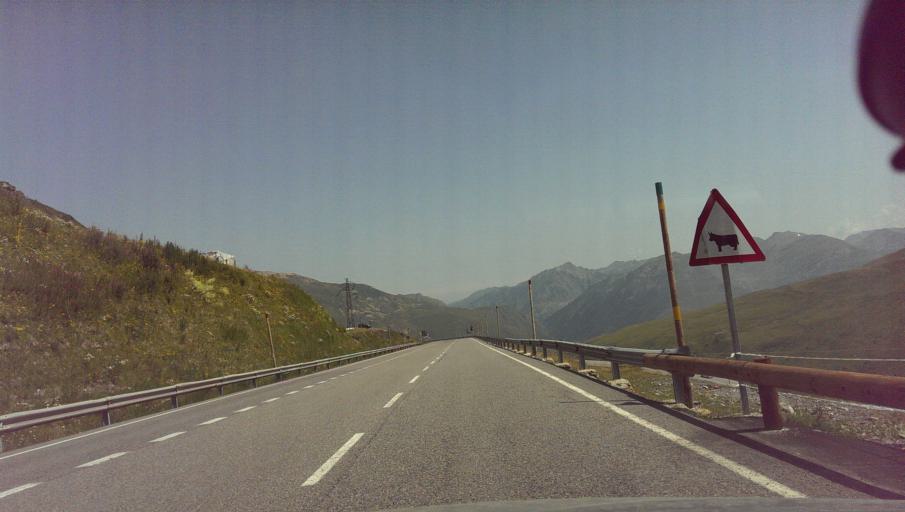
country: AD
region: Encamp
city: Pas de la Casa
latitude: 42.5392
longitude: 1.7230
